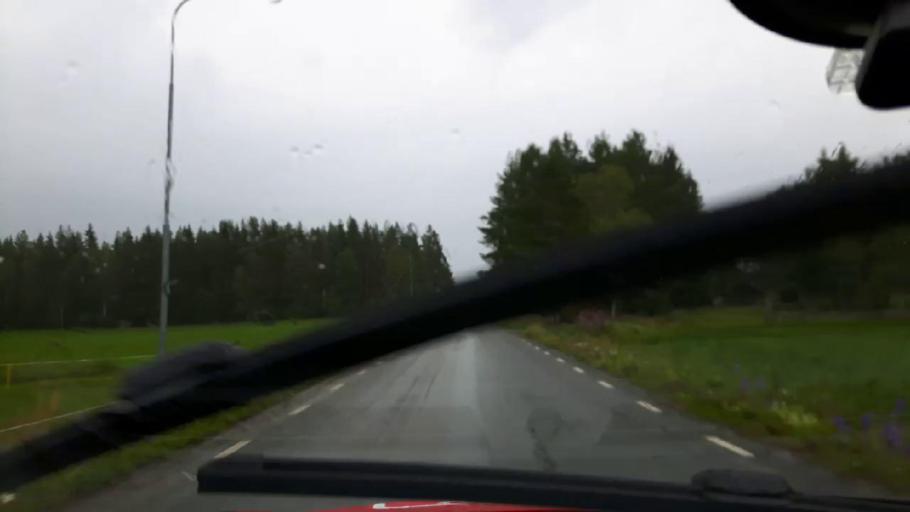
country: SE
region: Jaemtland
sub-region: OEstersunds Kommun
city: Brunflo
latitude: 62.9834
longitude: 14.8185
